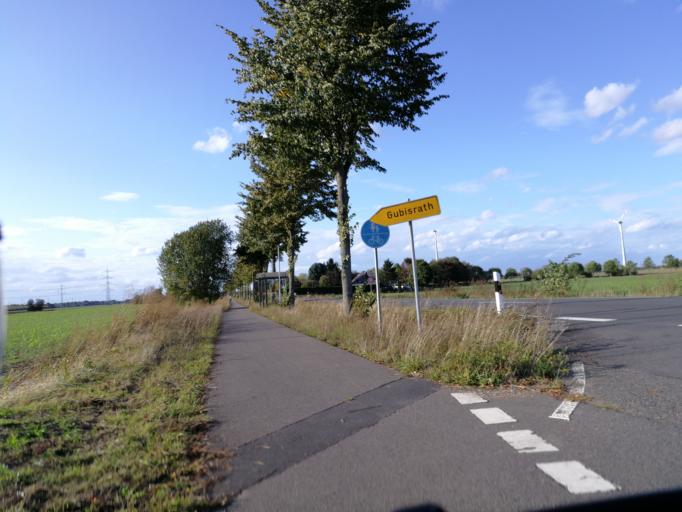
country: DE
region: North Rhine-Westphalia
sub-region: Regierungsbezirk Dusseldorf
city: Neubrueck
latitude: 51.1205
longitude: 6.7058
